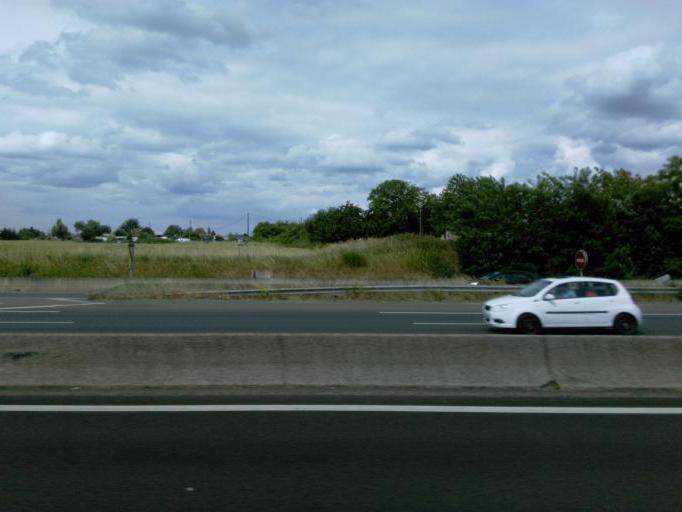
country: FR
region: Ile-de-France
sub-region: Departement du Val-d'Oise
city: Pierrelaye
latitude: 49.0104
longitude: 2.1546
